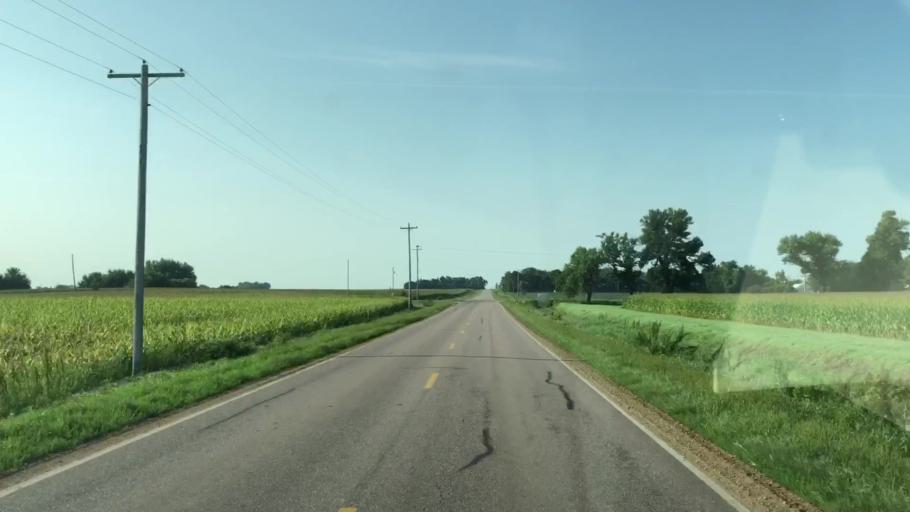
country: US
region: Iowa
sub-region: Lyon County
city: George
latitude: 43.2458
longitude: -96.0004
